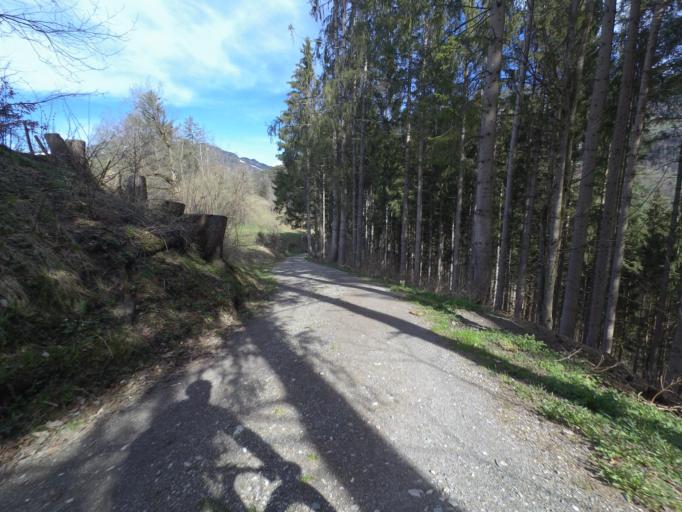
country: AT
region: Salzburg
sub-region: Politischer Bezirk Sankt Johann im Pongau
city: Sankt Veit im Pongau
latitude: 47.3259
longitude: 13.1357
